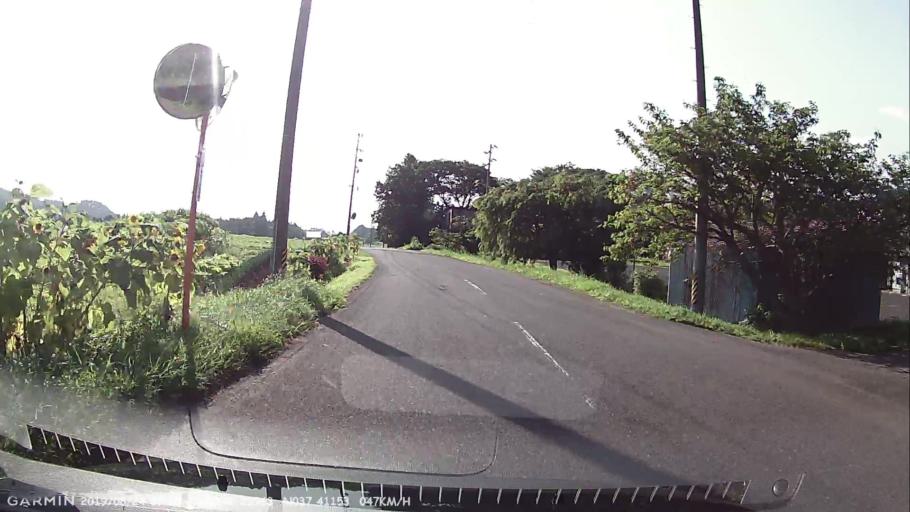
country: JP
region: Fukushima
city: Koriyama
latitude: 37.4115
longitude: 140.2398
